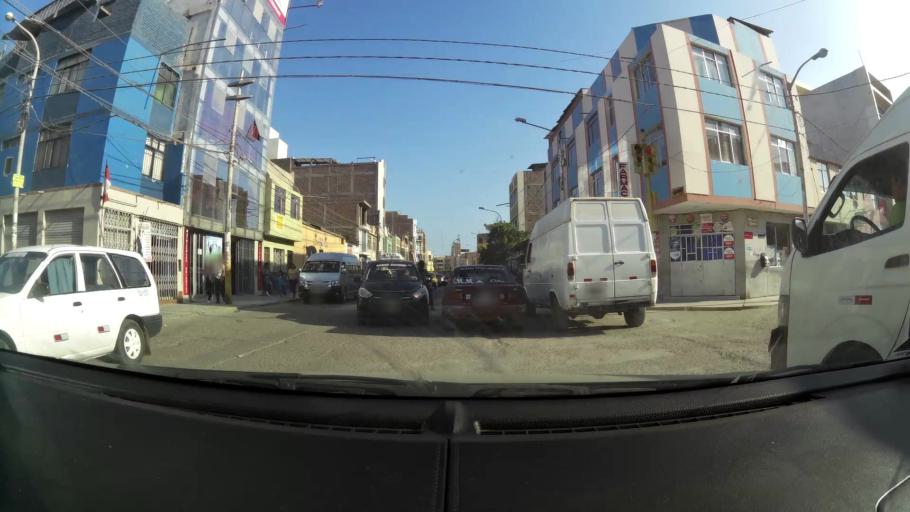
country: PE
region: Lambayeque
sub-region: Provincia de Chiclayo
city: Santa Rosa
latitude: -6.7680
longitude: -79.8357
